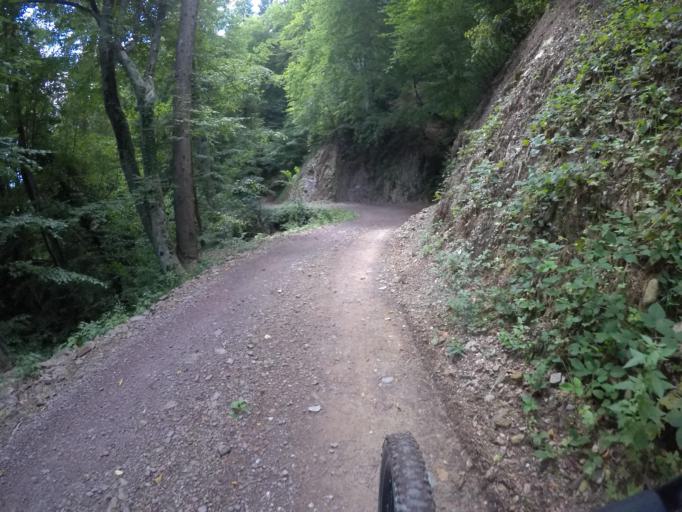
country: IT
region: Friuli Venezia Giulia
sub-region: Provincia di Udine
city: Arta Terme
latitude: 46.4798
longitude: 13.0611
